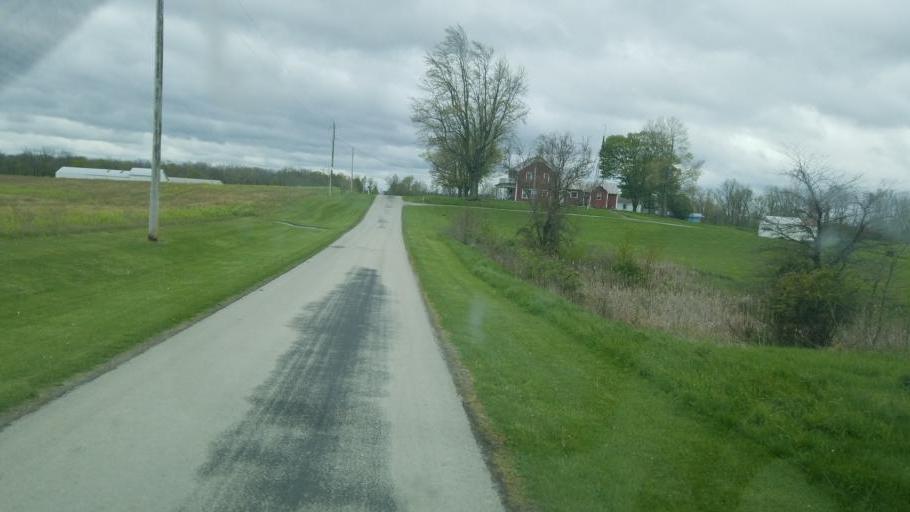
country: US
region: Ohio
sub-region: Wyandot County
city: Upper Sandusky
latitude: 40.7656
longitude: -83.1450
